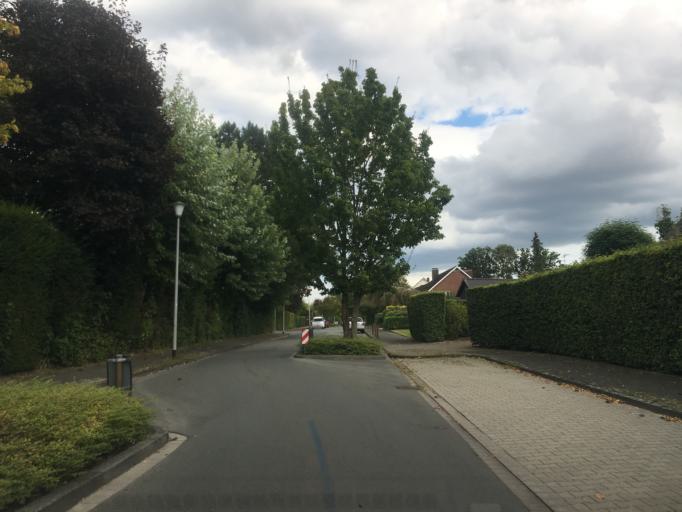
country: DE
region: North Rhine-Westphalia
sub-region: Regierungsbezirk Munster
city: Muenster
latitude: 51.9701
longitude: 7.5657
